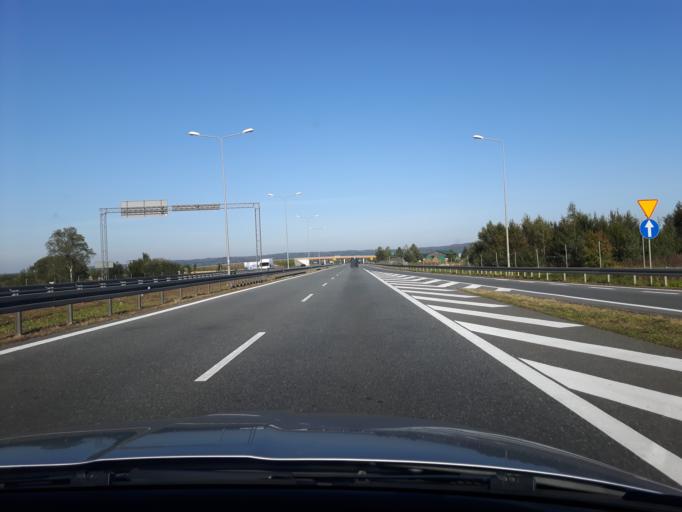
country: PL
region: Warmian-Masurian Voivodeship
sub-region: Powiat elblaski
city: Paslek
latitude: 54.0827
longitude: 19.6050
